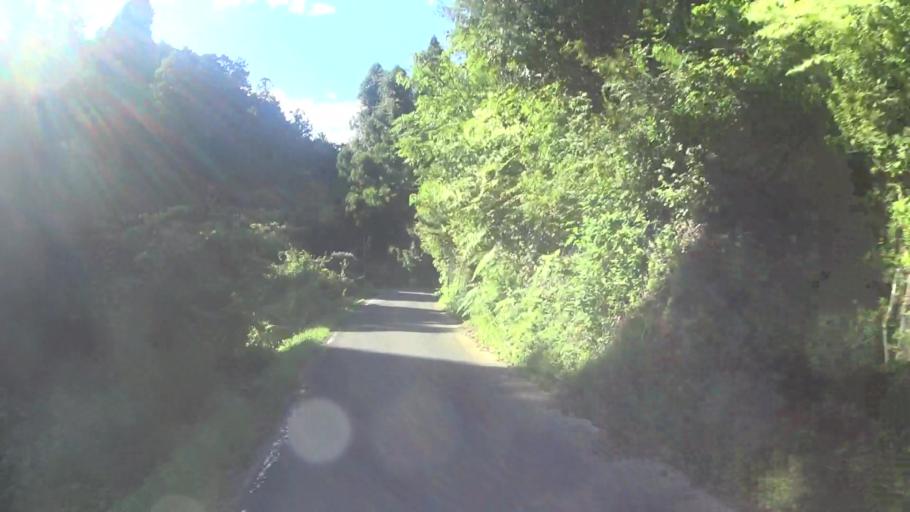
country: JP
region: Kyoto
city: Uji
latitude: 34.8260
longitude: 135.8844
